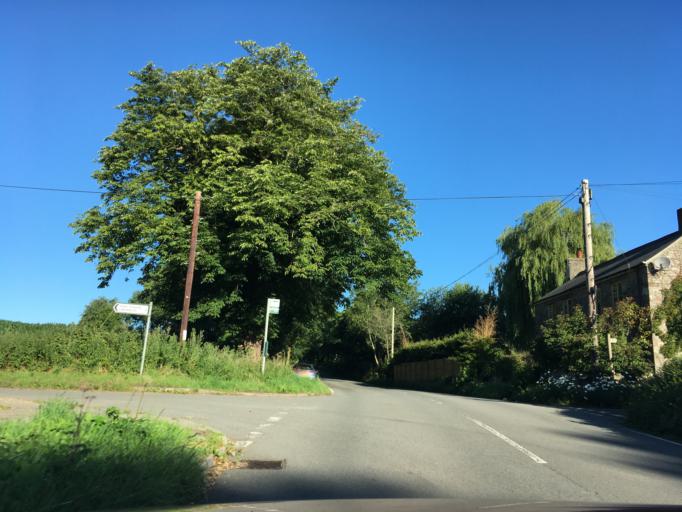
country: GB
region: Wales
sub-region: Monmouthshire
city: Chepstow
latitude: 51.6607
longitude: -2.7337
